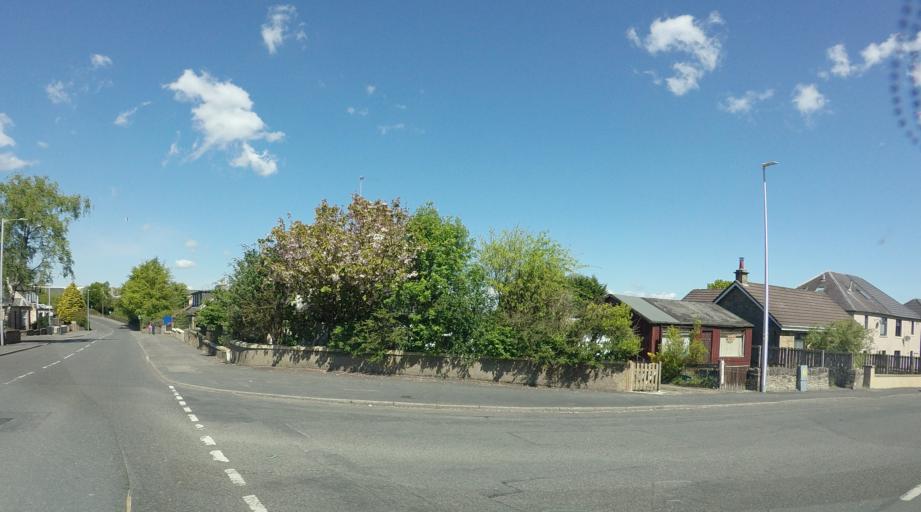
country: GB
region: Scotland
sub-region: Falkirk
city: Polmont
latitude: 55.9705
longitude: -3.6982
